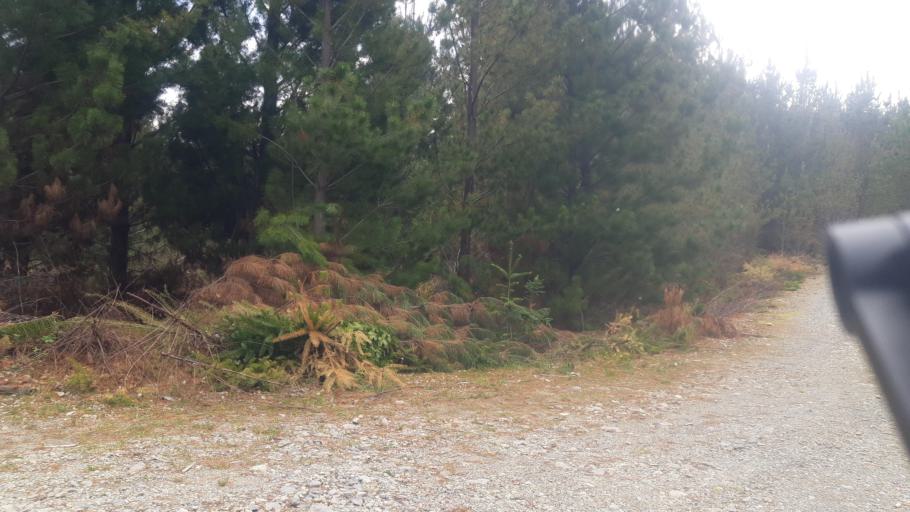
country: NZ
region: Tasman
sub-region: Tasman District
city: Wakefield
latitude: -41.7691
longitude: 172.8005
